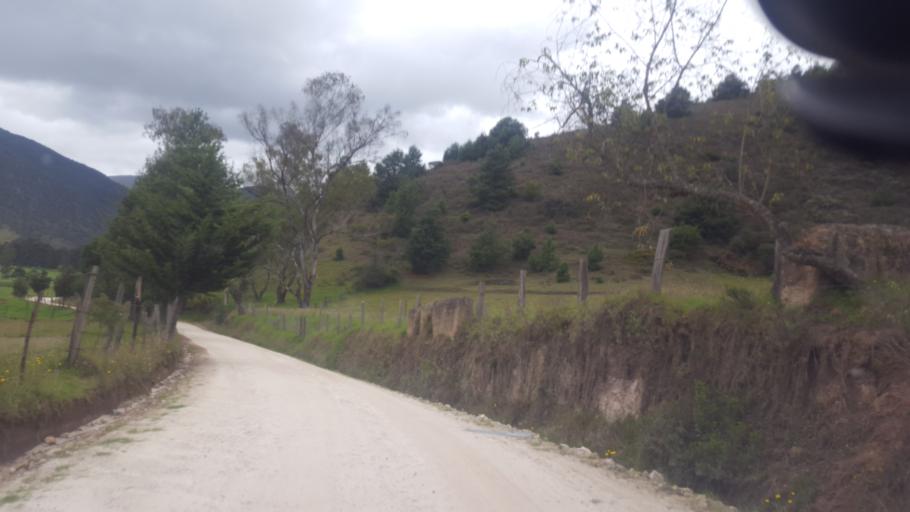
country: CO
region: Boyaca
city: Belen
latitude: 6.0005
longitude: -72.8481
